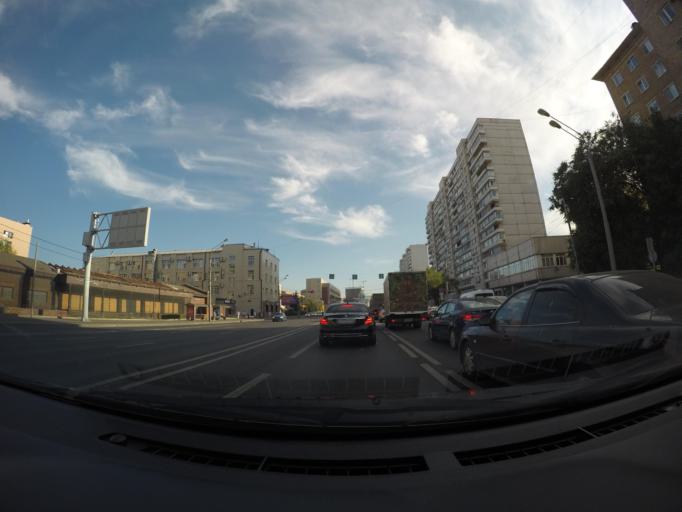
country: RU
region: Moscow
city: Mar'ina Roshcha
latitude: 55.8003
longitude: 37.5837
